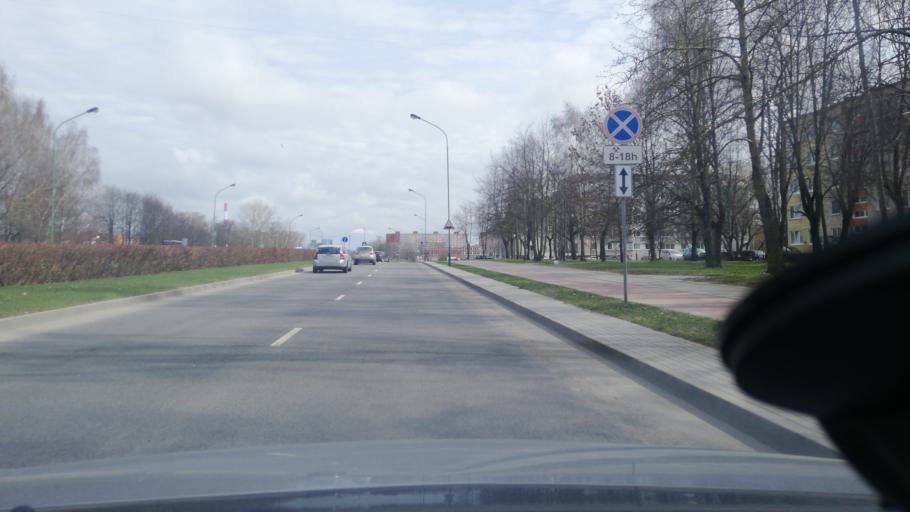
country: LT
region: Klaipedos apskritis
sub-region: Klaipeda
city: Klaipeda
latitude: 55.6742
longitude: 21.1765
